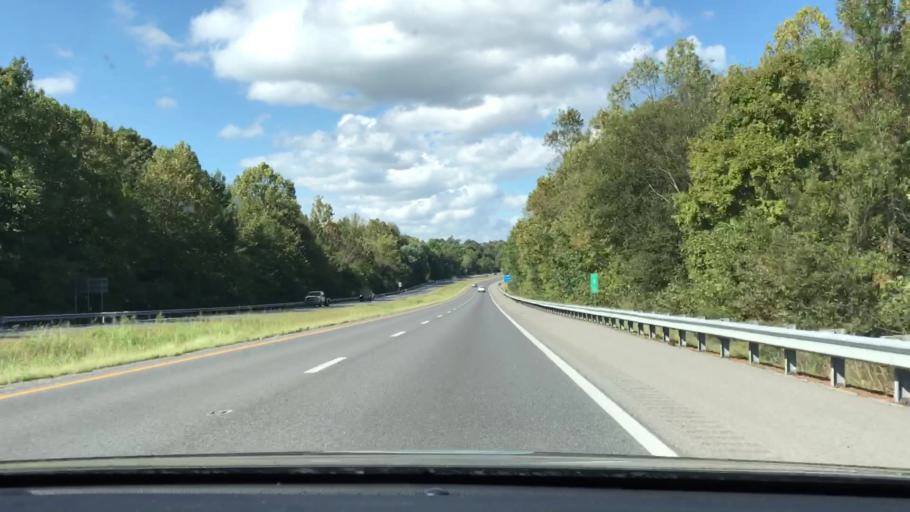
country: US
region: Kentucky
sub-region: Marshall County
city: Benton
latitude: 36.9150
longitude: -88.3504
